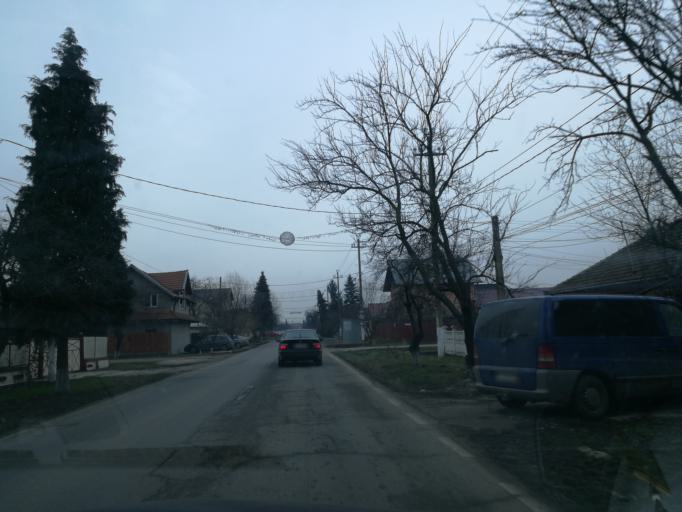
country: RO
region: Ilfov
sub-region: Comuna Gradistea
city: Gradistea
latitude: 44.6622
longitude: 26.3035
